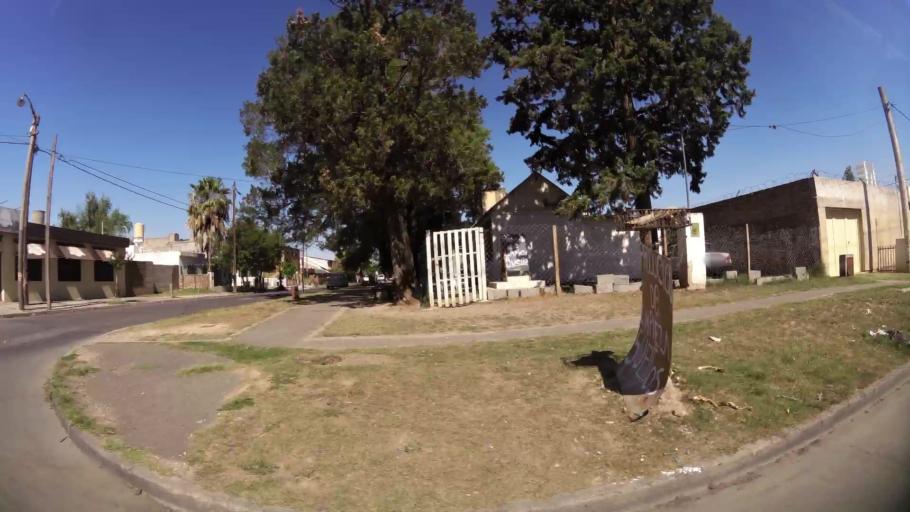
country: AR
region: Cordoba
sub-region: Departamento de Capital
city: Cordoba
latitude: -31.3768
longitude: -64.1678
